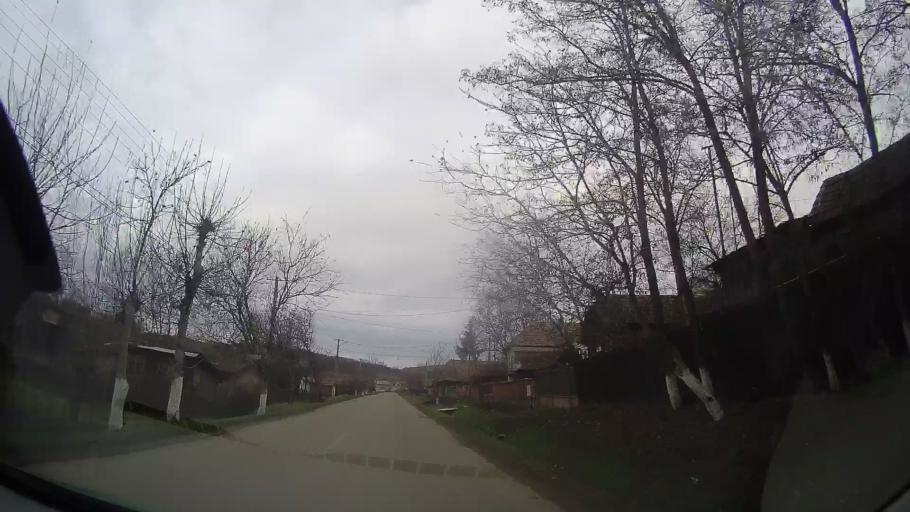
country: RO
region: Mures
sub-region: Comuna Faragau
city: Faragau
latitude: 46.7605
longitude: 24.5172
